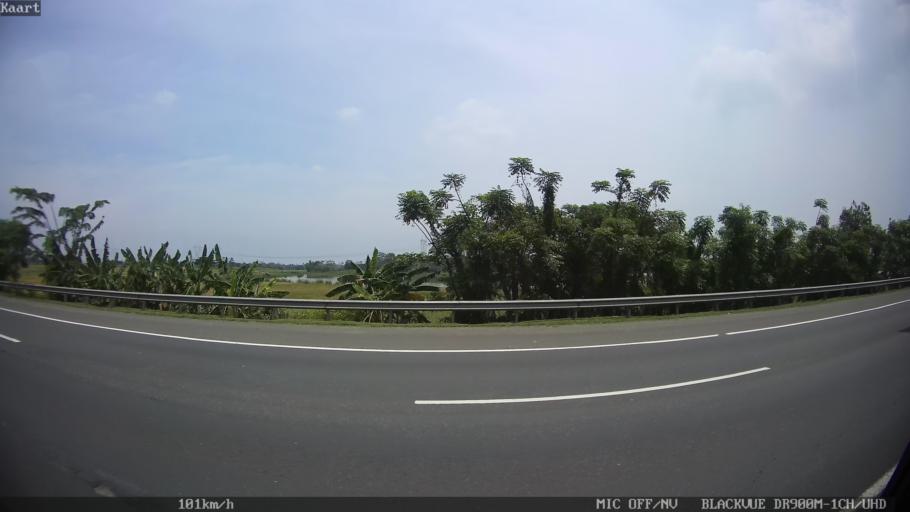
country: ID
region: West Java
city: Kresek
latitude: -6.1772
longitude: 106.3646
